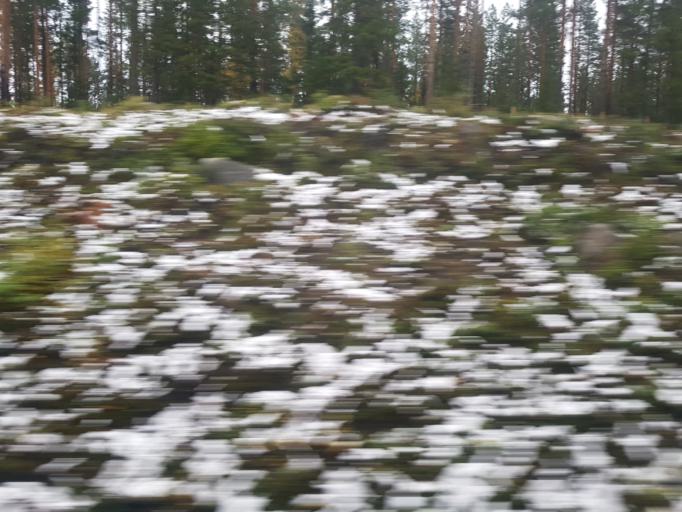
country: NO
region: Sor-Trondelag
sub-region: Rennebu
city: Berkak
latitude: 62.7155
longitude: 10.0324
